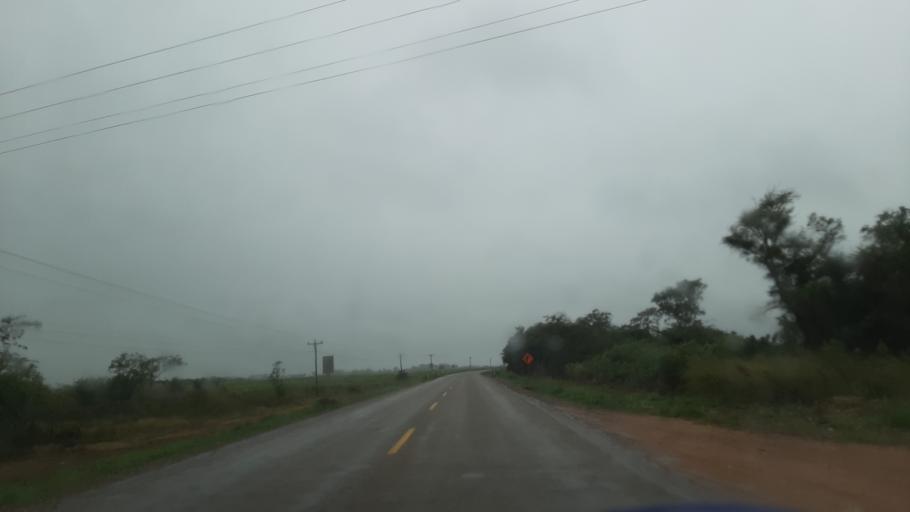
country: BO
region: Santa Cruz
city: Okinawa Numero Uno
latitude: -16.8264
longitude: -62.6055
